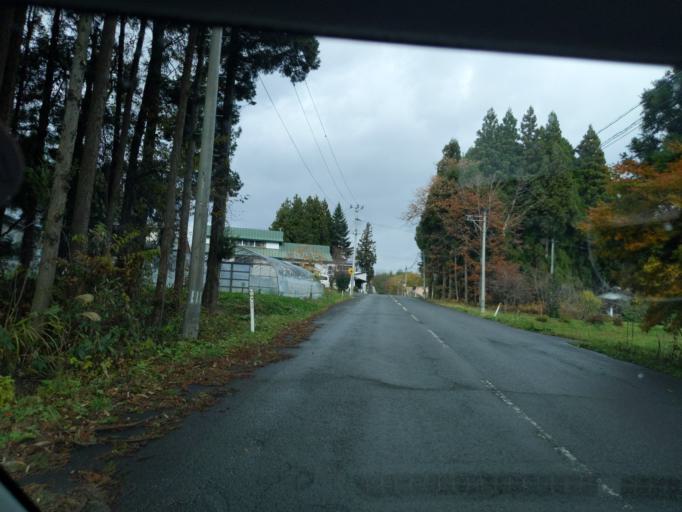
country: JP
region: Iwate
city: Mizusawa
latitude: 39.1059
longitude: 140.9878
